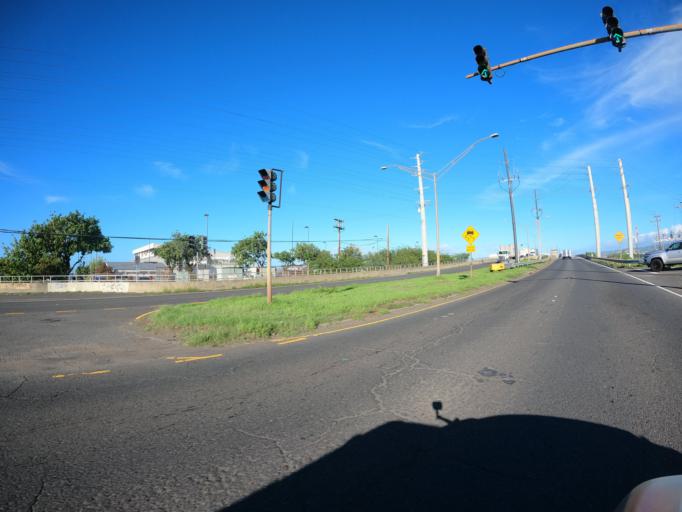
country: US
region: Hawaii
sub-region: Honolulu County
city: Honolulu
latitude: 21.3130
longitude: -157.8872
